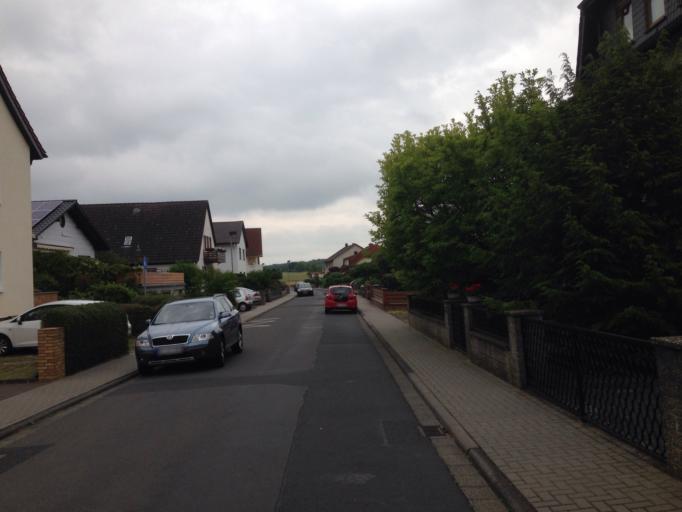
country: DE
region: Hesse
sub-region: Regierungsbezirk Giessen
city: Grossen Buseck
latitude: 50.5743
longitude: 8.7523
